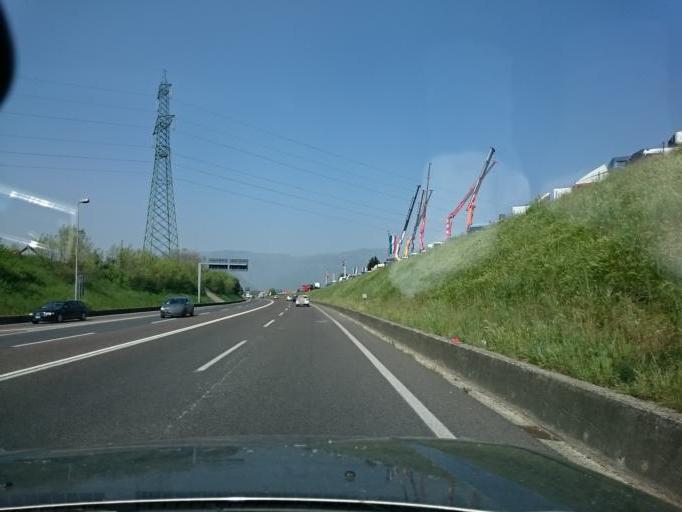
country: IT
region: Veneto
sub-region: Provincia di Vicenza
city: San Zeno-San Giuseppe
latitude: 45.7521
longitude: 11.7761
